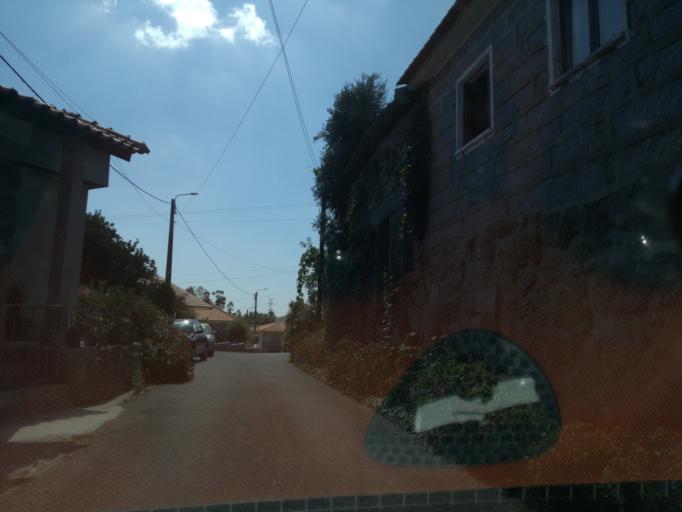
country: PT
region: Braga
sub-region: Fafe
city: Aroes
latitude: 41.4944
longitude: -8.2296
